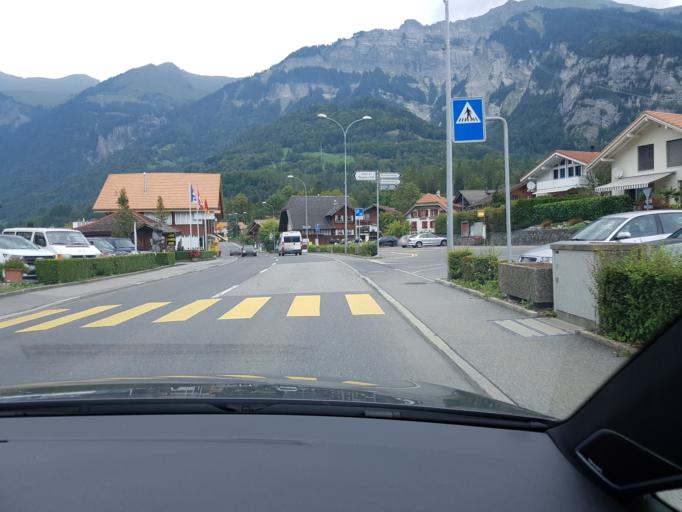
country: CH
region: Bern
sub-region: Interlaken-Oberhasli District
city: Brienz
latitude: 46.7495
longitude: 8.0530
